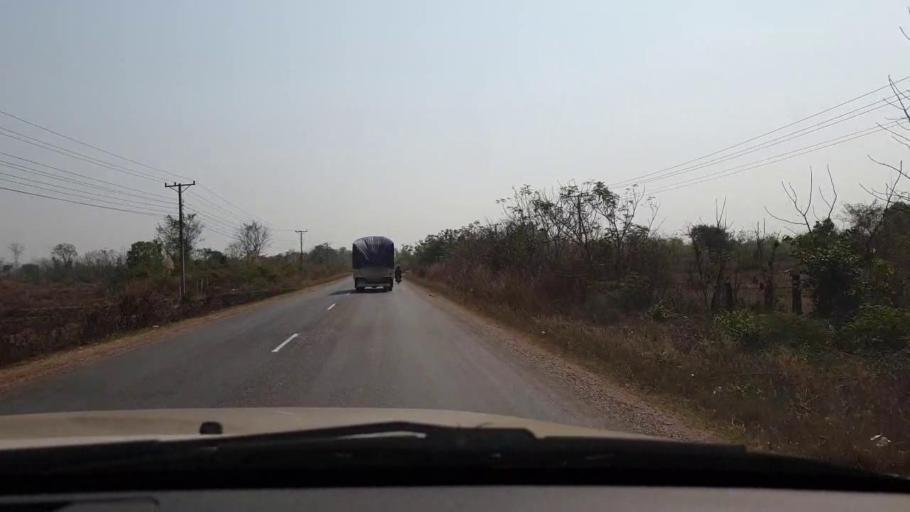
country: TH
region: Nong Khai
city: Phon Phisai
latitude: 18.0774
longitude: 102.9518
